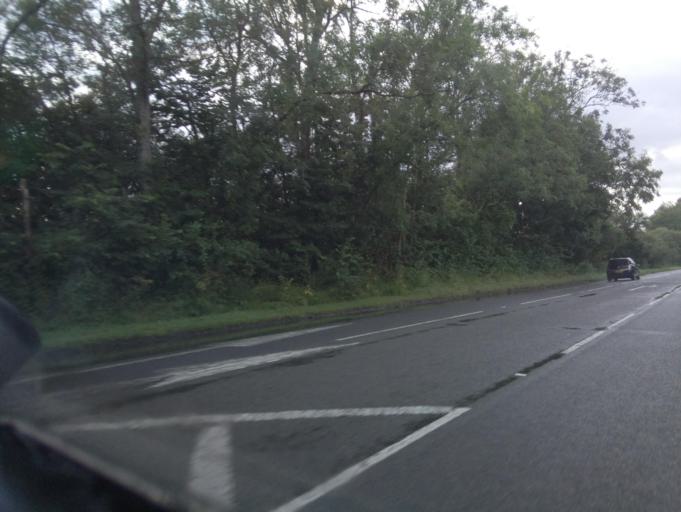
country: GB
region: England
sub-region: Oxfordshire
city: Kidlington
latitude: 51.8335
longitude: -1.3031
